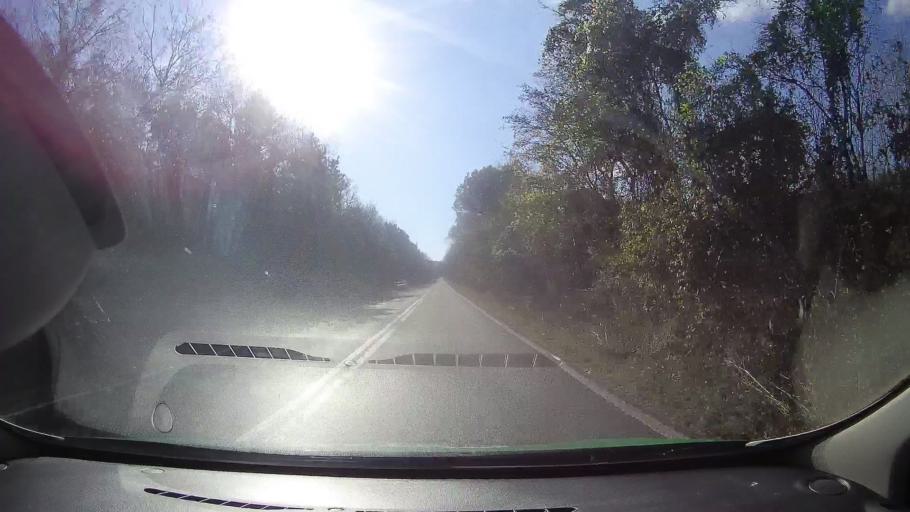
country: RO
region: Tulcea
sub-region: Oras Babadag
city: Babadag
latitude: 44.8374
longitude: 28.6956
